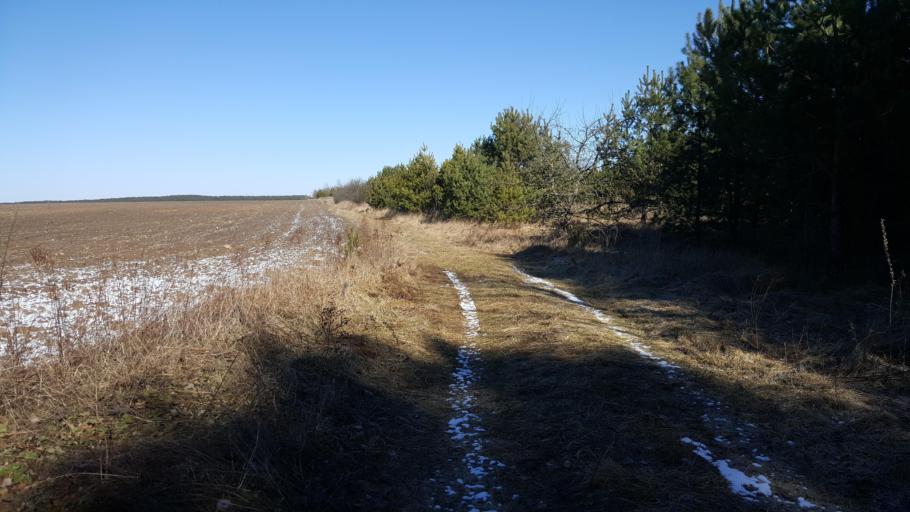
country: BY
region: Brest
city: Kamyanyets
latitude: 52.3663
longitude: 23.8304
